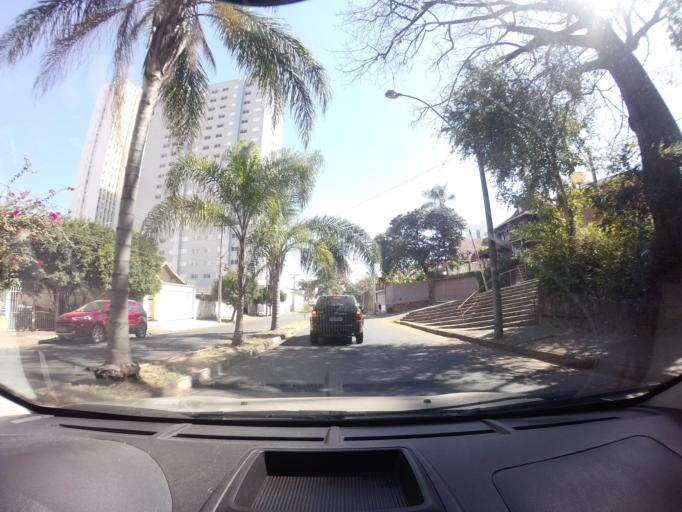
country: BR
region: Sao Paulo
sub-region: Piracicaba
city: Piracicaba
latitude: -22.7175
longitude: -47.6448
